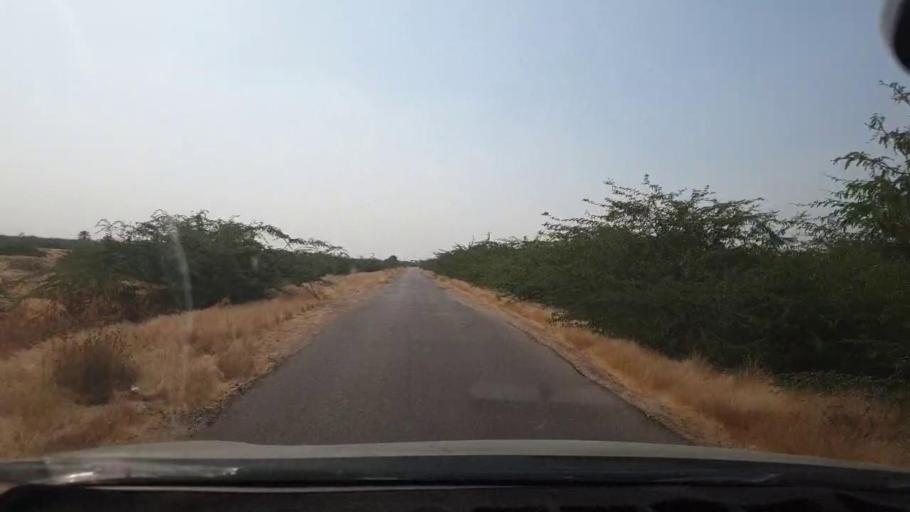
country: PK
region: Sindh
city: Malir Cantonment
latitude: 25.1042
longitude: 67.1980
